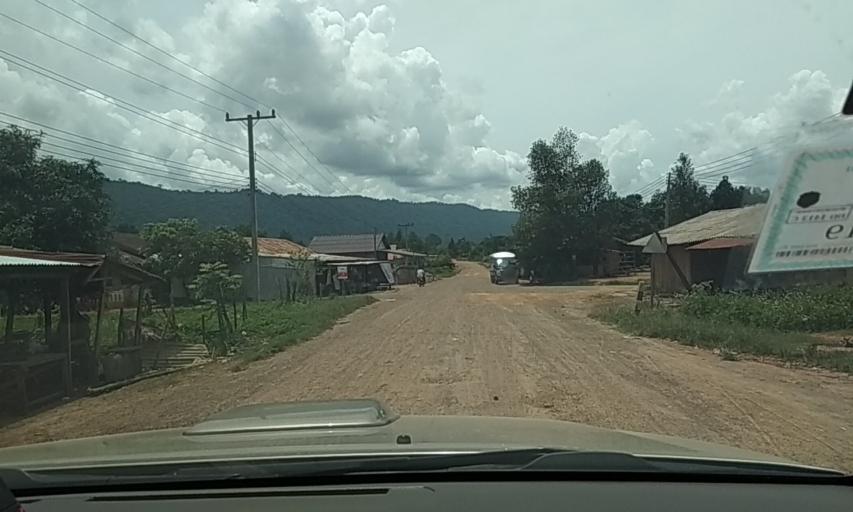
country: LA
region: Bolikhamxai
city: Ban Nahin
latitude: 18.1400
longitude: 104.7616
